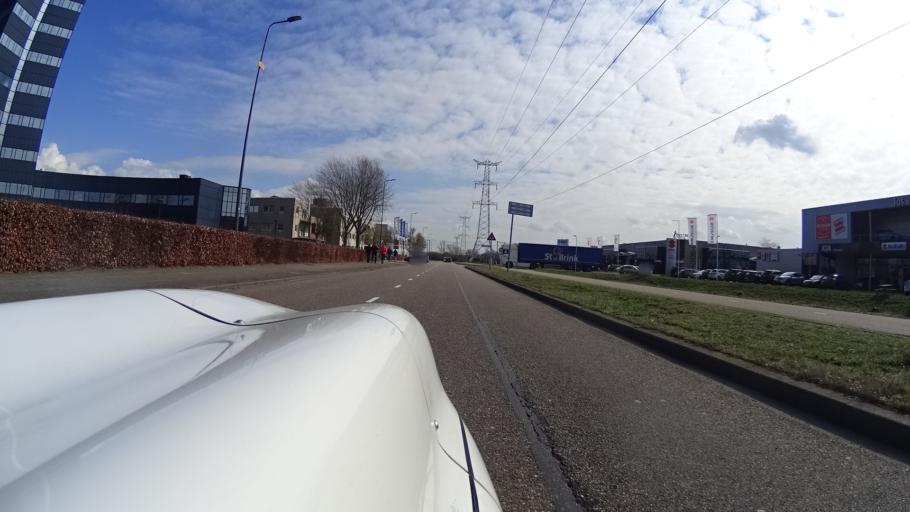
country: NL
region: North Brabant
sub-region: Gemeente 's-Hertogenbosch
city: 's-Hertogenbosch
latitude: 51.7082
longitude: 5.3390
